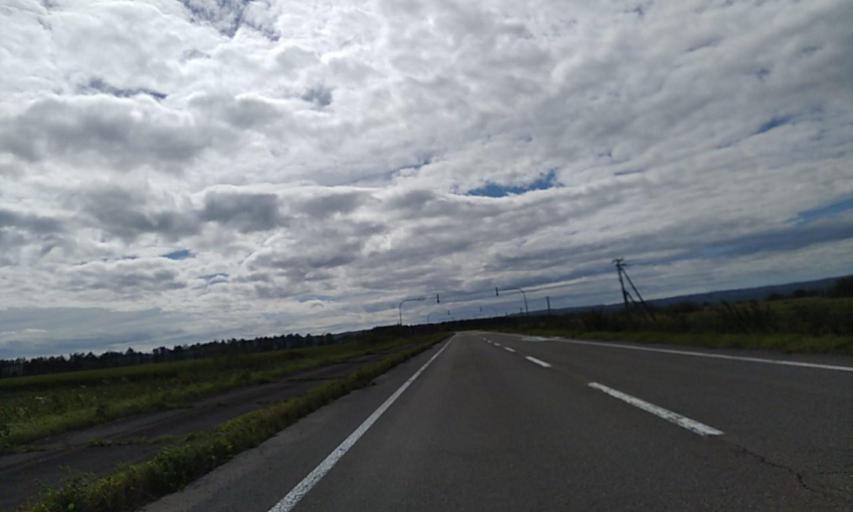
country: JP
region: Hokkaido
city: Obihiro
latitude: 42.7183
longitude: 143.6456
